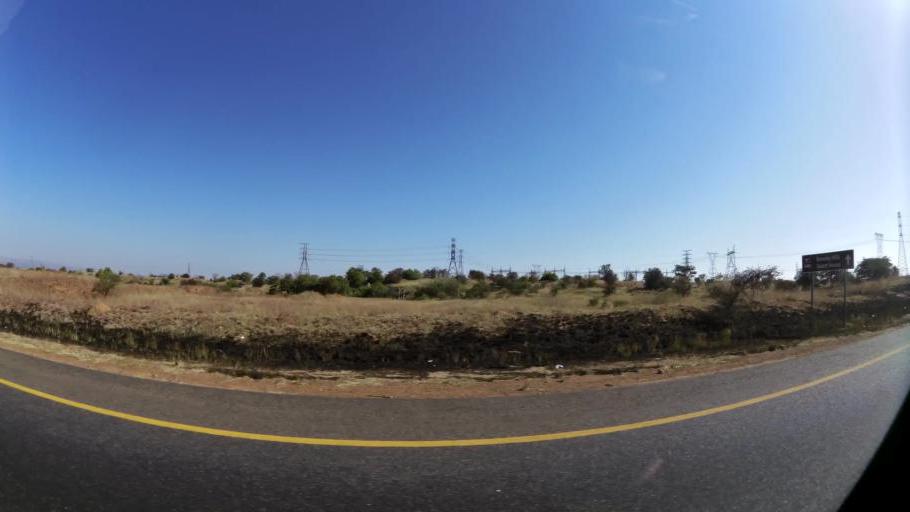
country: ZA
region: Gauteng
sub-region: City of Tshwane Metropolitan Municipality
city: Mabopane
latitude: -25.5639
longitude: 28.1075
